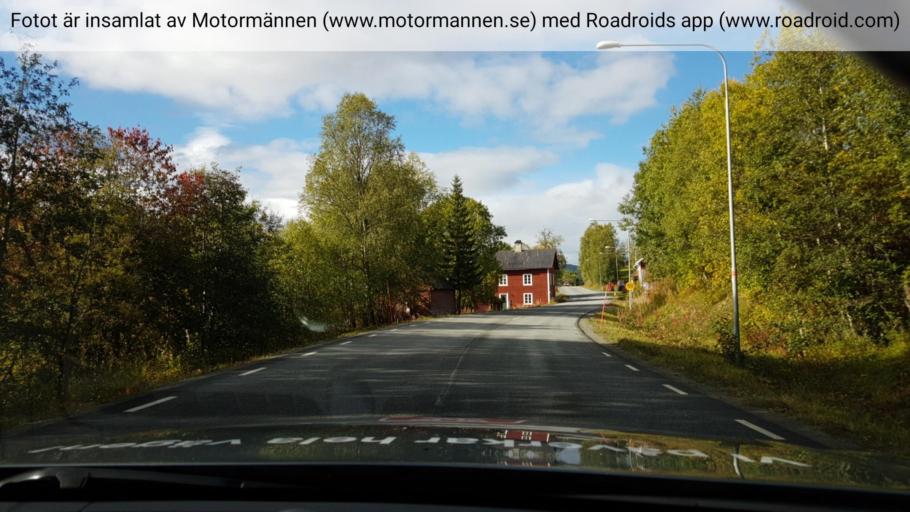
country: SE
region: Jaemtland
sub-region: Are Kommun
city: Are
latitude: 63.3952
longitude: 12.9644
